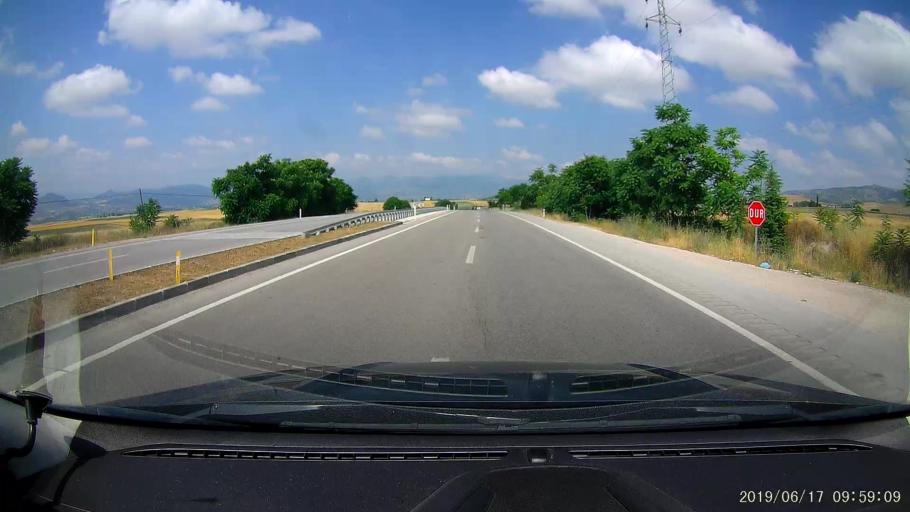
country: TR
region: Amasya
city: Alicik
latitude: 40.8681
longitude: 35.3221
